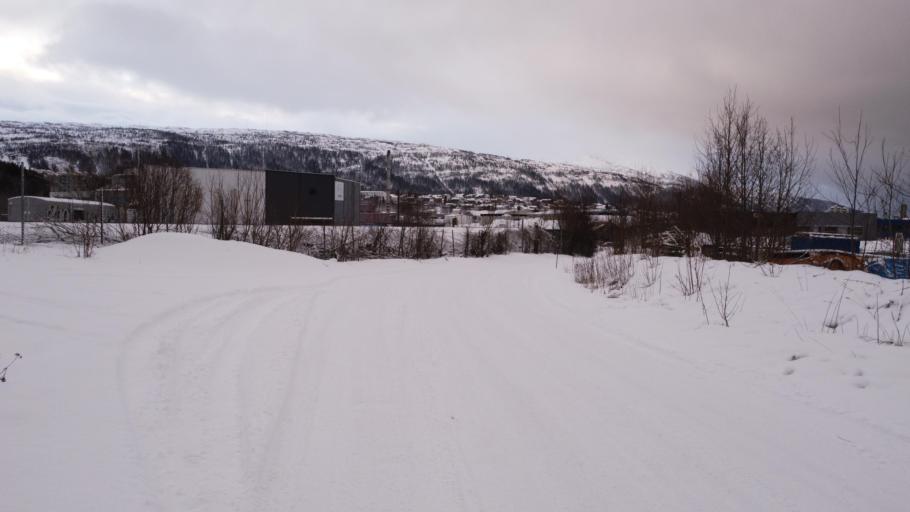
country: NO
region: Nordland
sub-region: Rana
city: Mo i Rana
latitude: 66.3255
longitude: 14.1525
